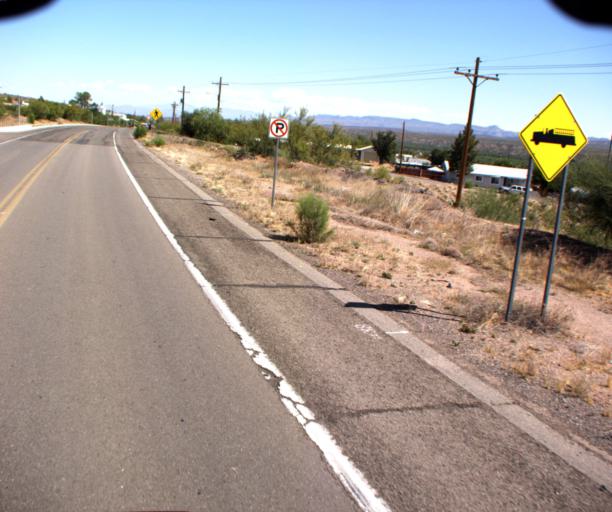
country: US
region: Arizona
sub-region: Pinal County
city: Mammoth
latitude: 32.7184
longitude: -110.6433
